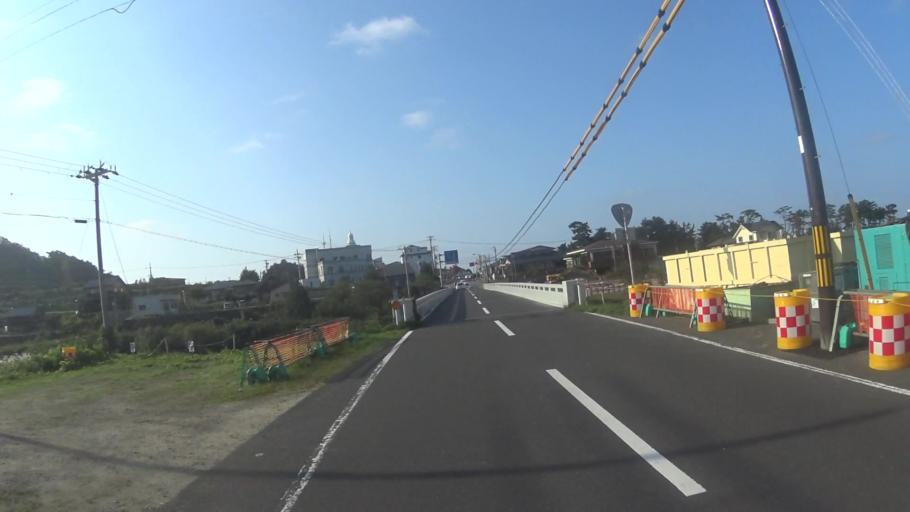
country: JP
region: Kyoto
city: Miyazu
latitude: 35.7381
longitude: 135.1045
